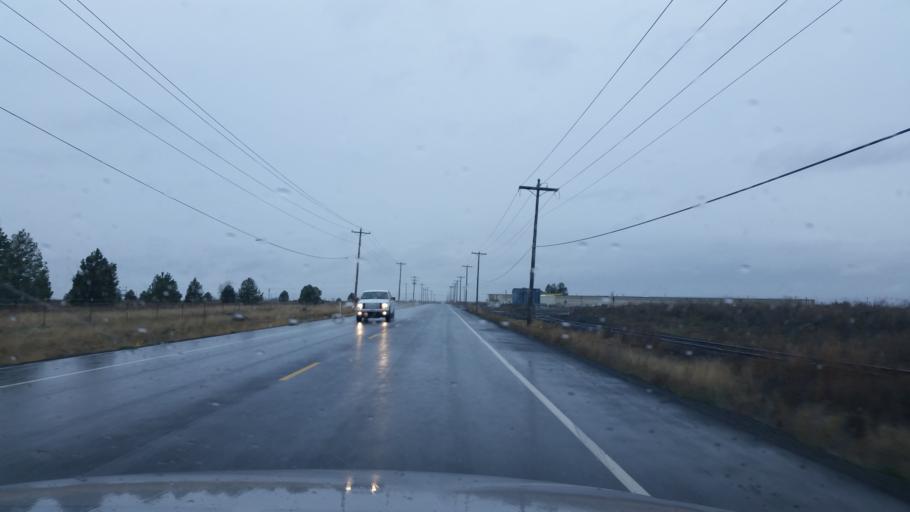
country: US
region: Washington
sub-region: Spokane County
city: Airway Heights
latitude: 47.6284
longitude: -117.5967
